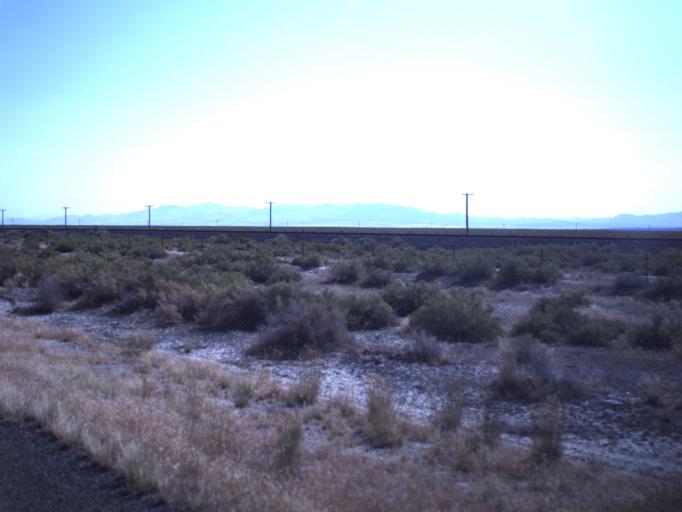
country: US
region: Utah
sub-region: Millard County
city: Delta
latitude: 39.1268
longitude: -112.7340
